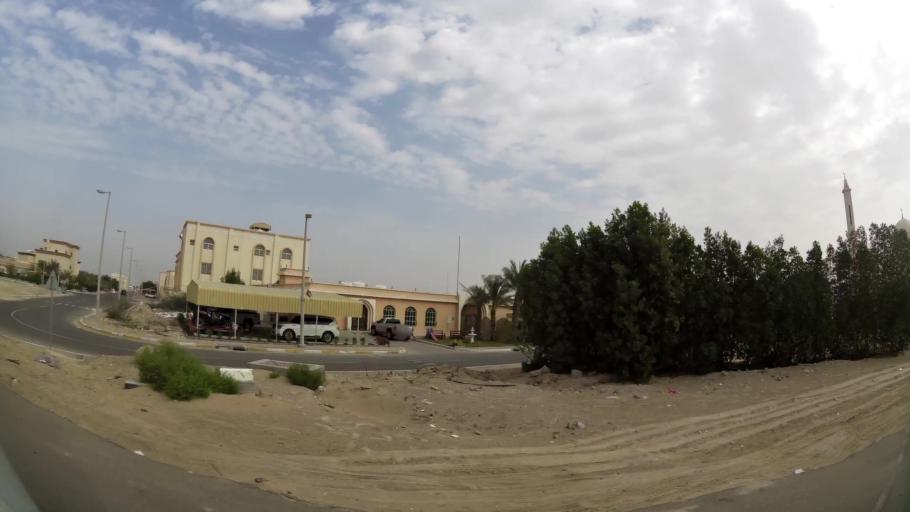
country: AE
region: Abu Dhabi
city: Abu Dhabi
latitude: 24.3125
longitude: 54.6391
